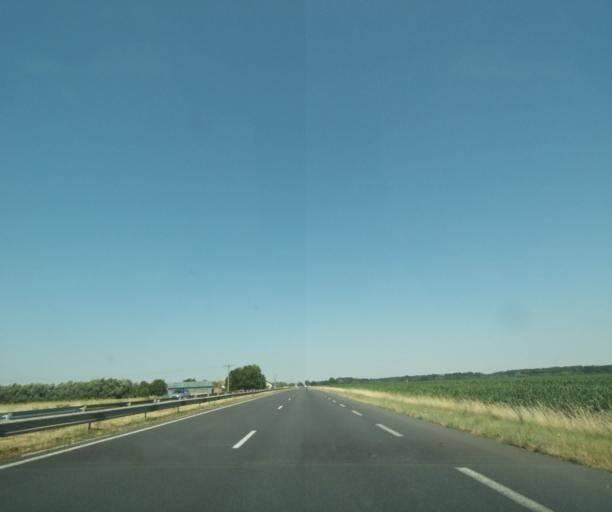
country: FR
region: Champagne-Ardenne
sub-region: Departement de la Haute-Marne
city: Villiers-en-Lieu
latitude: 48.6618
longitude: 4.7996
